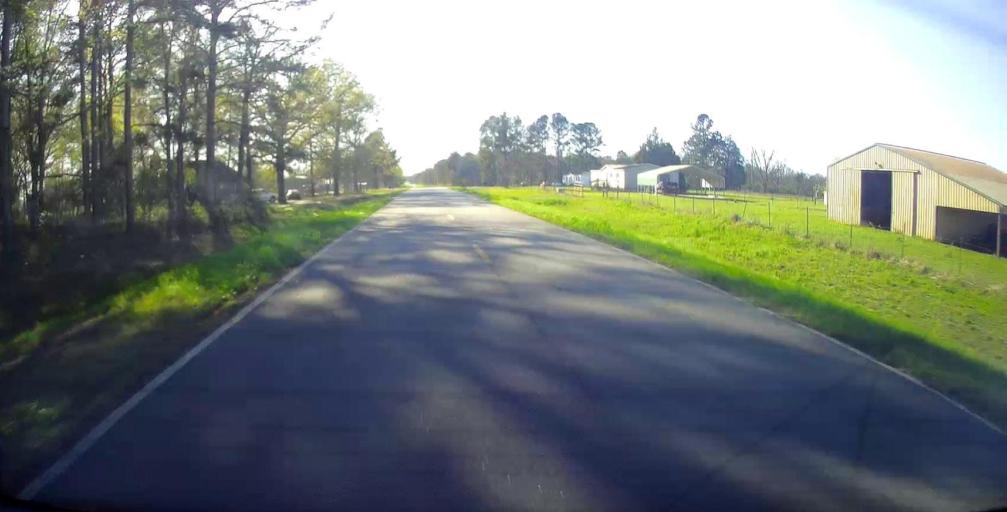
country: US
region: Georgia
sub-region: Pulaski County
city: Hawkinsville
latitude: 32.3477
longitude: -83.5906
